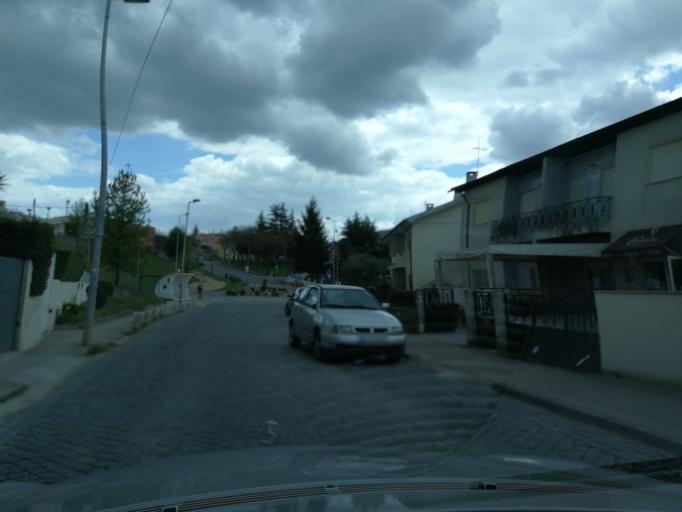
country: PT
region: Braga
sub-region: Braga
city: Braga
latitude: 41.5342
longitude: -8.4176
